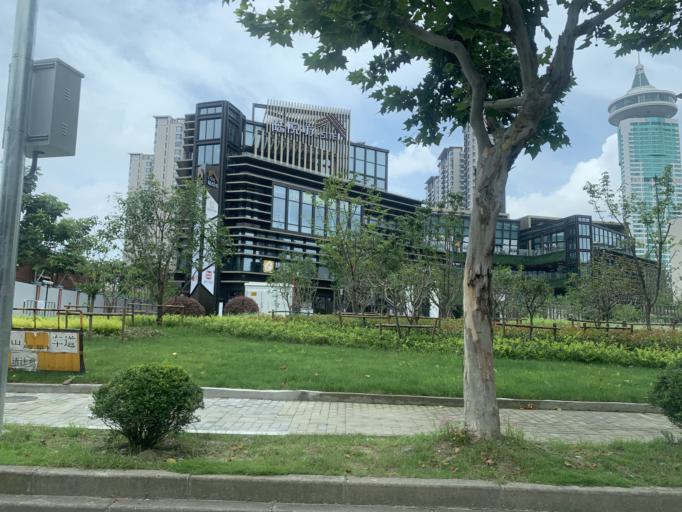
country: CN
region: Shanghai Shi
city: Huamu
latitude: 31.2105
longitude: 121.5328
